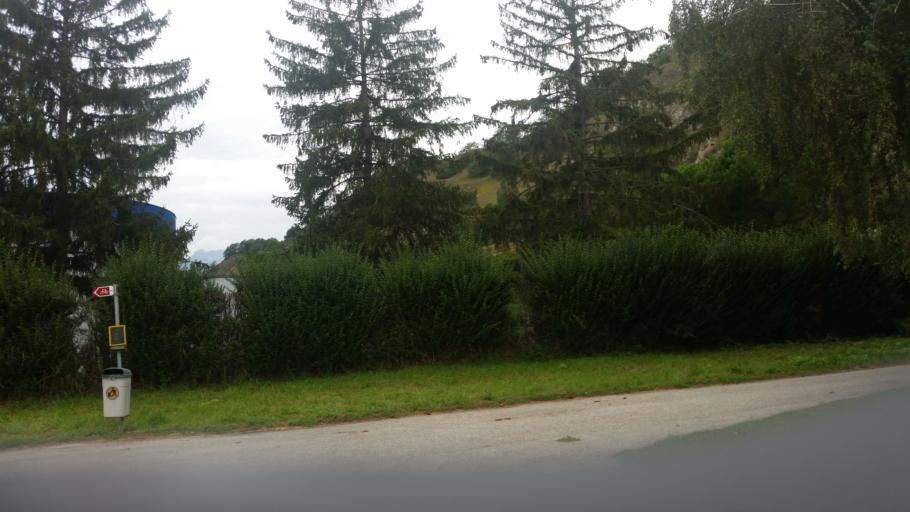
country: CH
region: Valais
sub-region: Conthey District
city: Conthey
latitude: 46.2213
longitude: 7.3201
